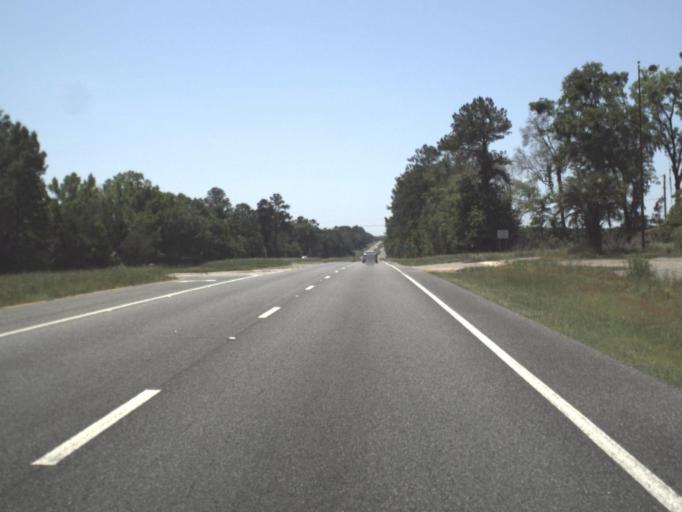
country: US
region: Florida
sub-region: Jefferson County
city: Monticello
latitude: 30.6627
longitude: -83.8787
